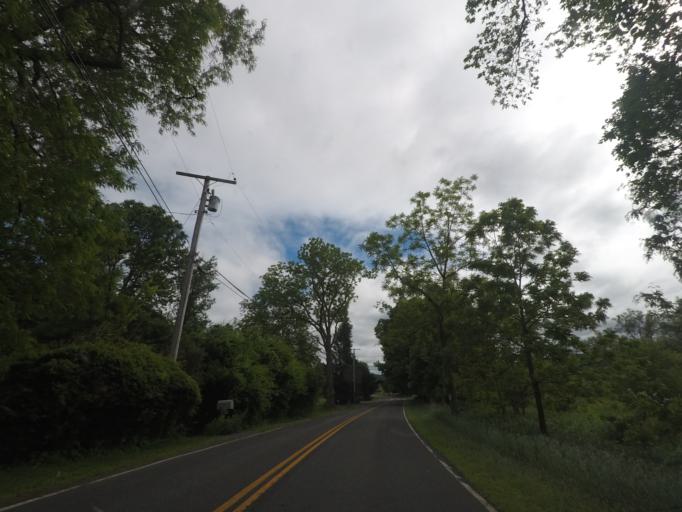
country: US
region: New York
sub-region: Dutchess County
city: Pine Plains
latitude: 42.0319
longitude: -73.5141
